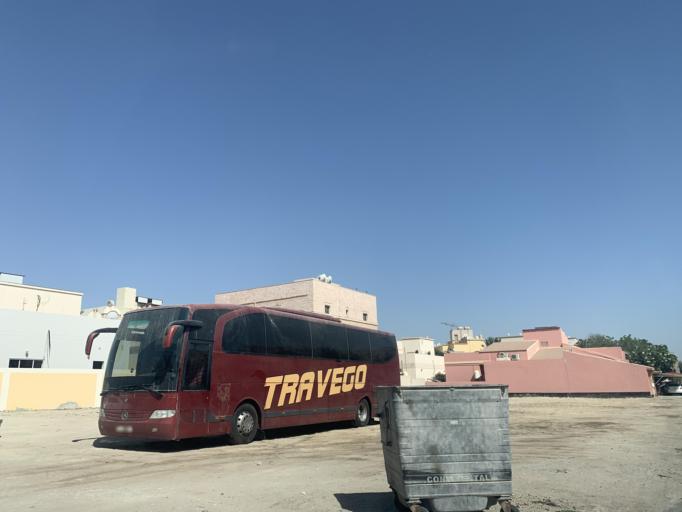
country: BH
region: Manama
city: Jidd Hafs
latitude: 26.2241
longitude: 50.5282
